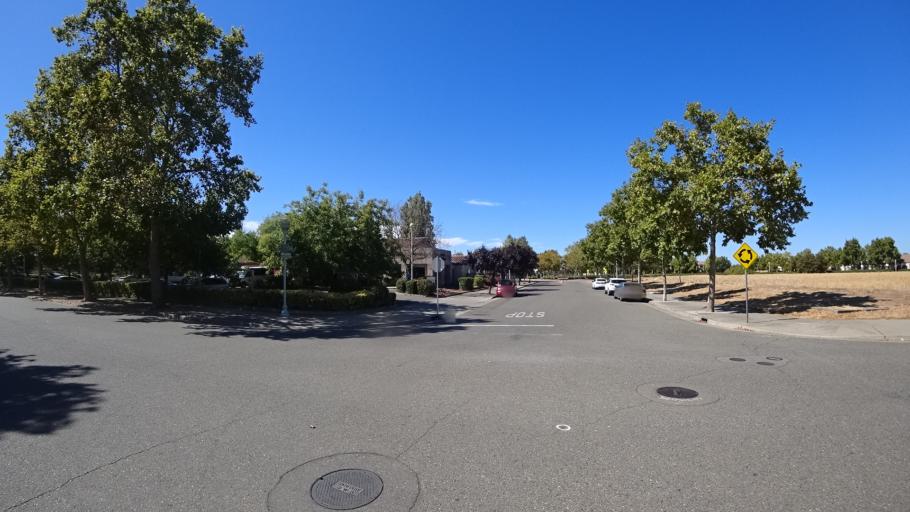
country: US
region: California
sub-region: Sacramento County
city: Laguna
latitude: 38.4253
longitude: -121.4686
